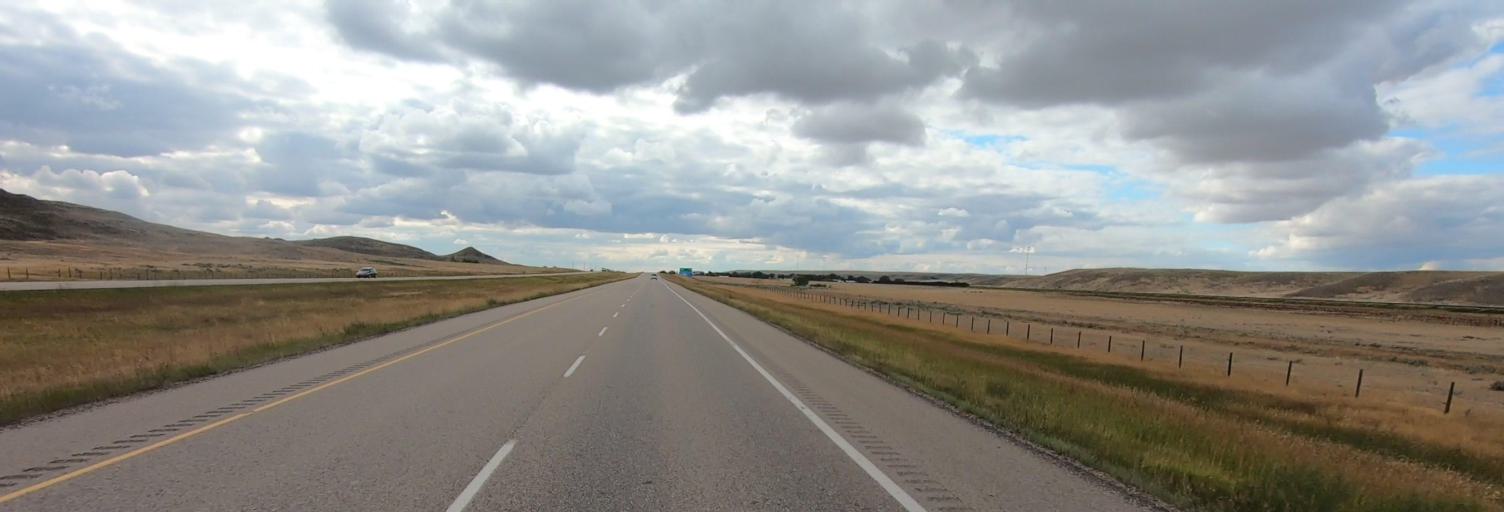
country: CA
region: Alberta
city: Medicine Hat
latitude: 49.9525
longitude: -110.2483
